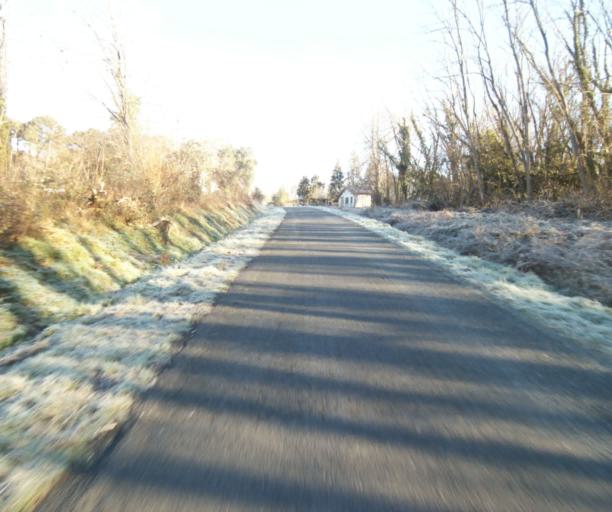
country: FR
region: Aquitaine
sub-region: Departement des Landes
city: Gabarret
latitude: 44.1116
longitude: 0.0800
